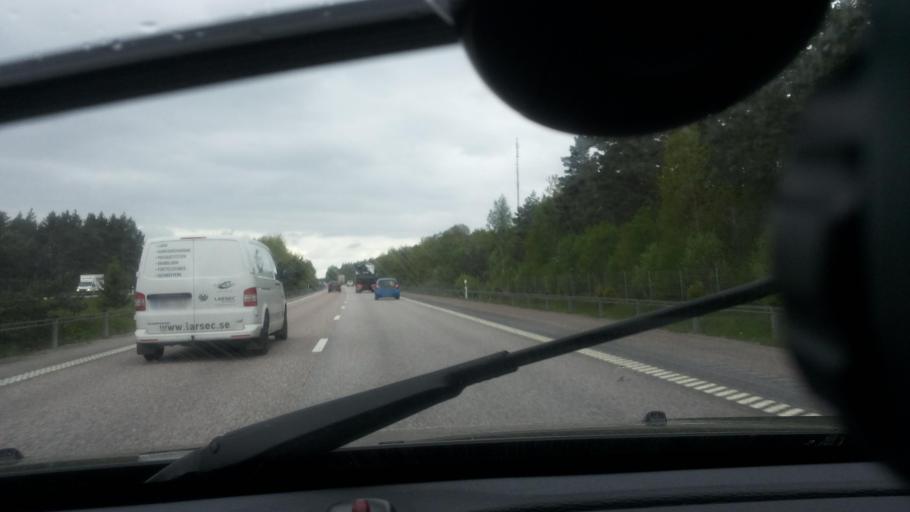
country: SE
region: Stockholm
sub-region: Sigtuna Kommun
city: Marsta
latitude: 59.6623
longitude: 17.8829
